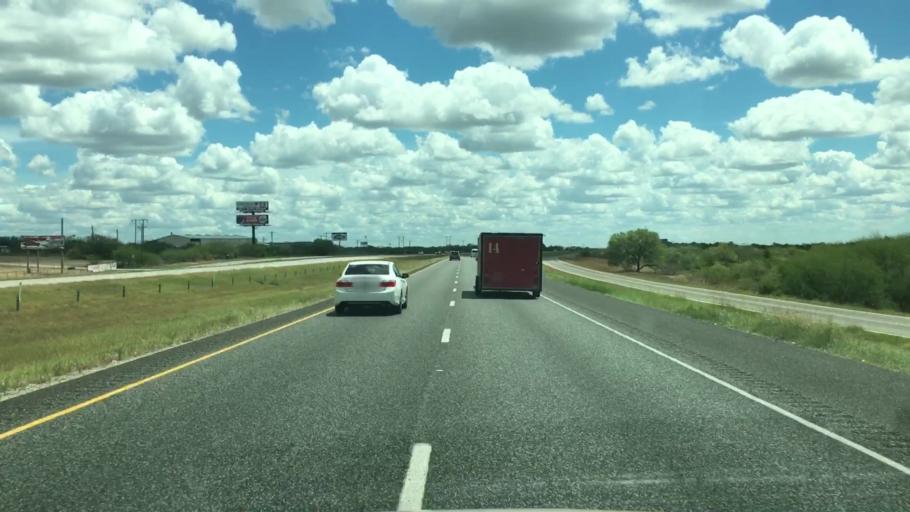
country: US
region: Texas
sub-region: Atascosa County
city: Pleasanton
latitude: 28.8888
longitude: -98.4076
